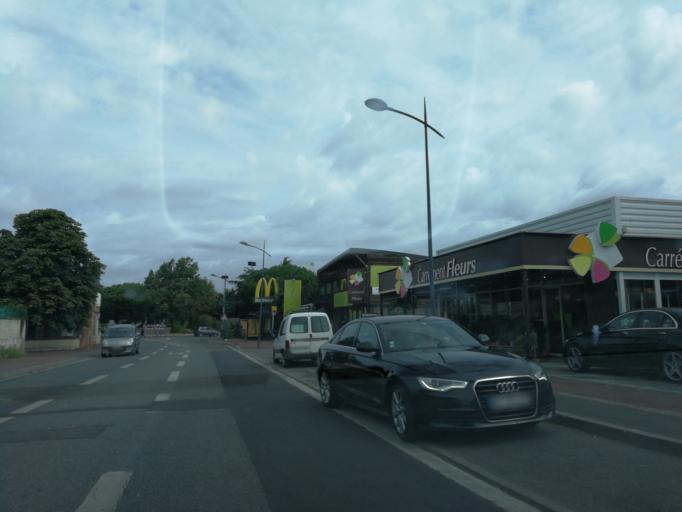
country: FR
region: Midi-Pyrenees
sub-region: Departement de la Haute-Garonne
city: Aucamville
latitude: 43.6608
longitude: 1.4316
